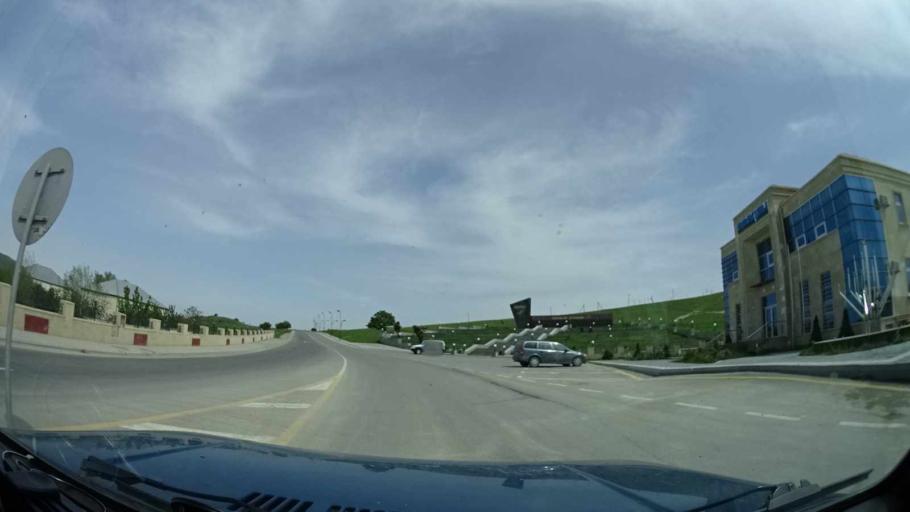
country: AZ
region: Xizi
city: Khyzy
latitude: 40.9101
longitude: 49.0757
